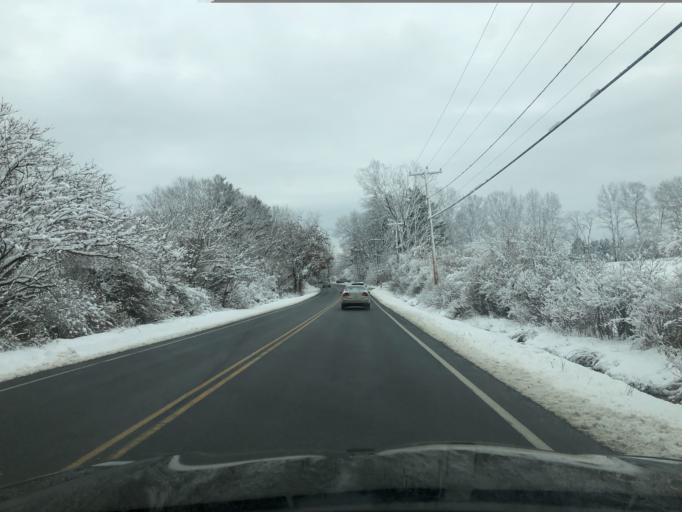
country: US
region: New Hampshire
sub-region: Strafford County
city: Dover
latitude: 43.2231
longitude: -70.8626
